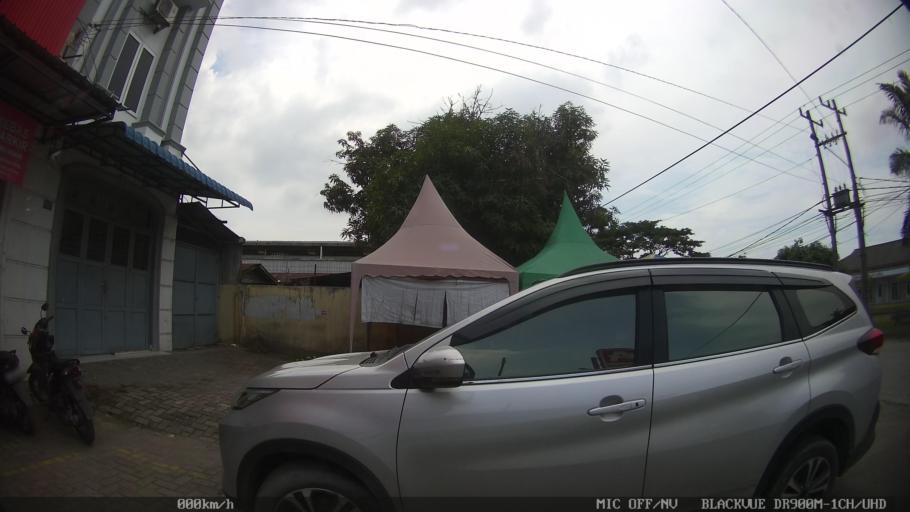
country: ID
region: North Sumatra
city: Medan
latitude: 3.6426
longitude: 98.6777
